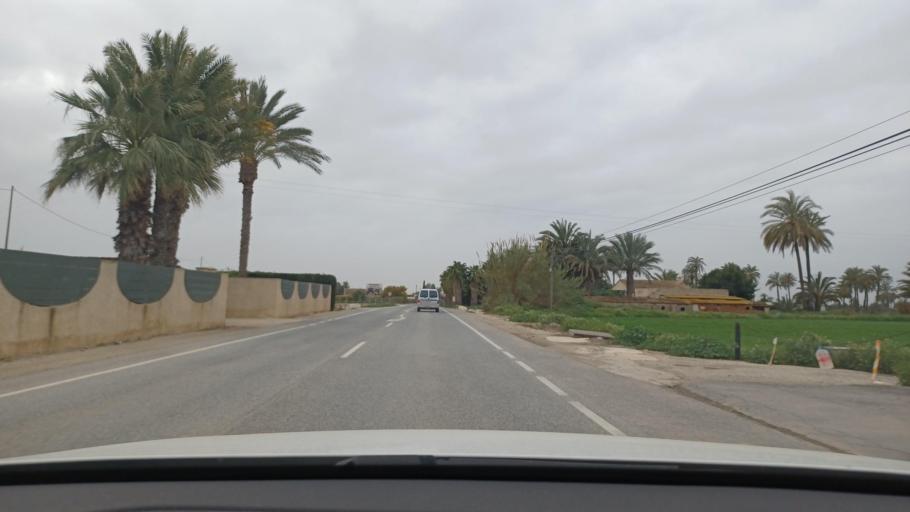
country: ES
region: Valencia
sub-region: Provincia de Alicante
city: Elche
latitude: 38.2297
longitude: -0.7180
